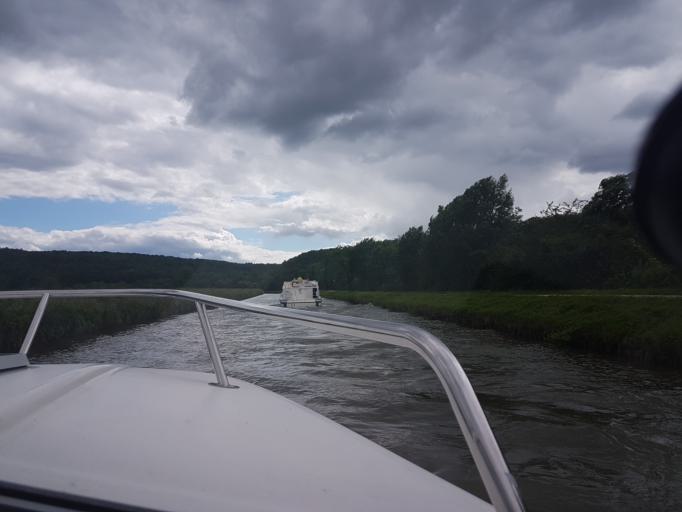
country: FR
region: Bourgogne
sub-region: Departement de l'Yonne
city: Vermenton
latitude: 47.5714
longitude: 3.6403
